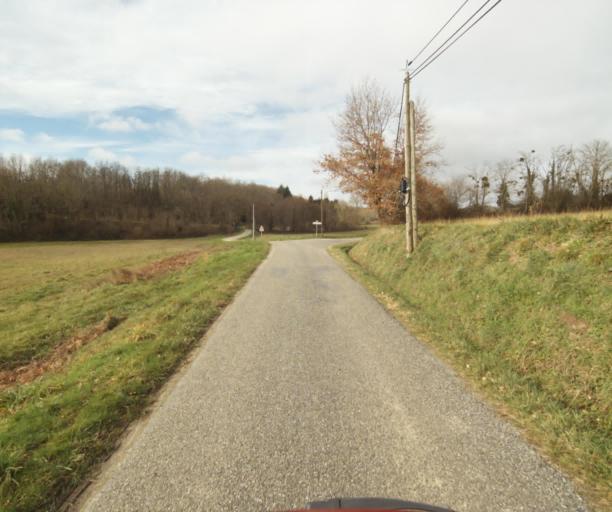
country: FR
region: Midi-Pyrenees
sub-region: Departement de l'Ariege
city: Pamiers
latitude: 43.1020
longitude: 1.5235
